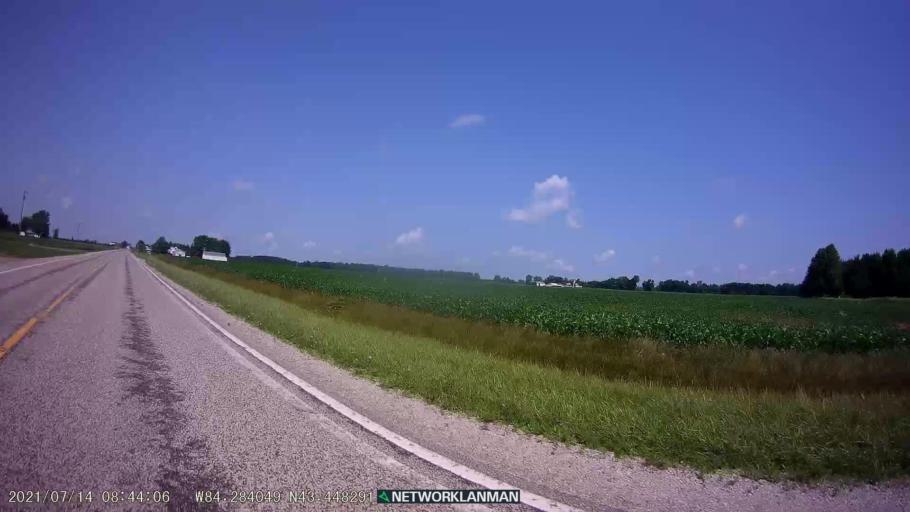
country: US
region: Michigan
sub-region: Saginaw County
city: Hemlock
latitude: 43.4484
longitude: -84.2844
